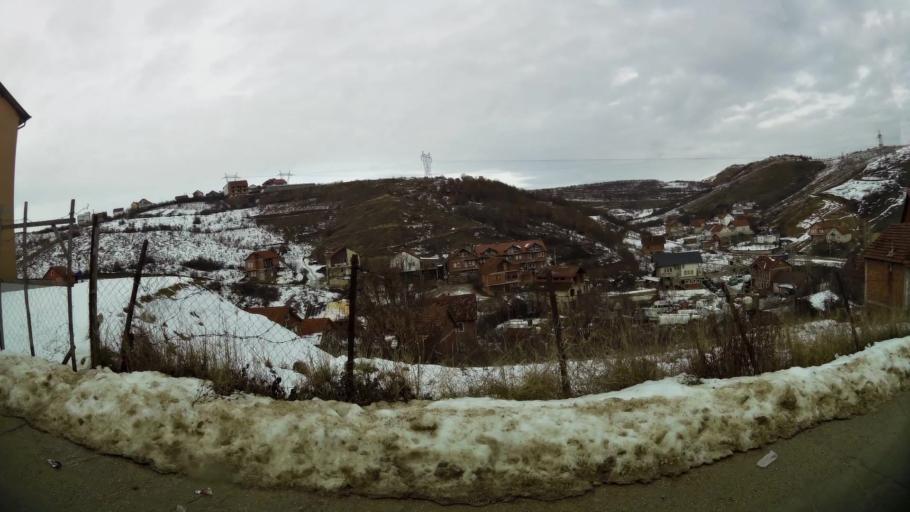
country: XK
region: Pristina
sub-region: Komuna e Prishtines
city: Pristina
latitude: 42.6907
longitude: 21.1735
